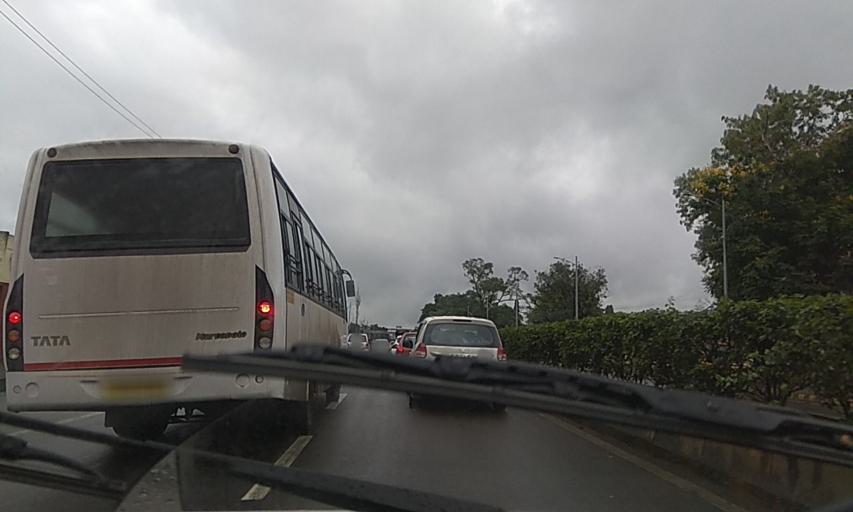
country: IN
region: Maharashtra
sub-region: Pune Division
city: Khadki
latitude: 18.5523
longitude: 73.8656
